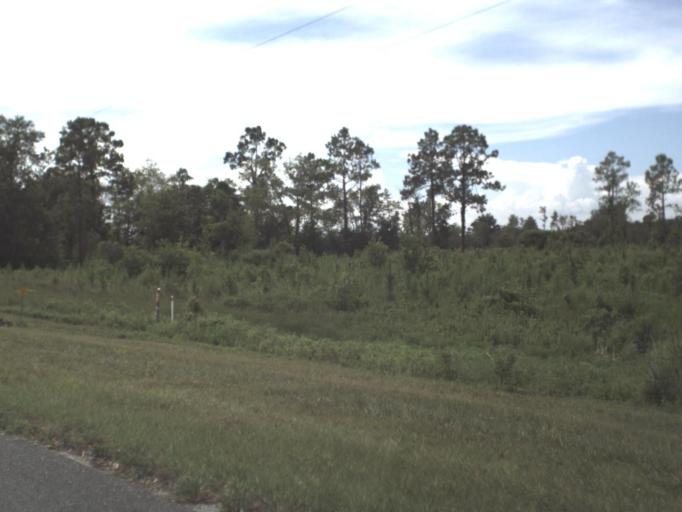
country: US
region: Florida
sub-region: Taylor County
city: Perry
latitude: 30.0811
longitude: -83.5067
